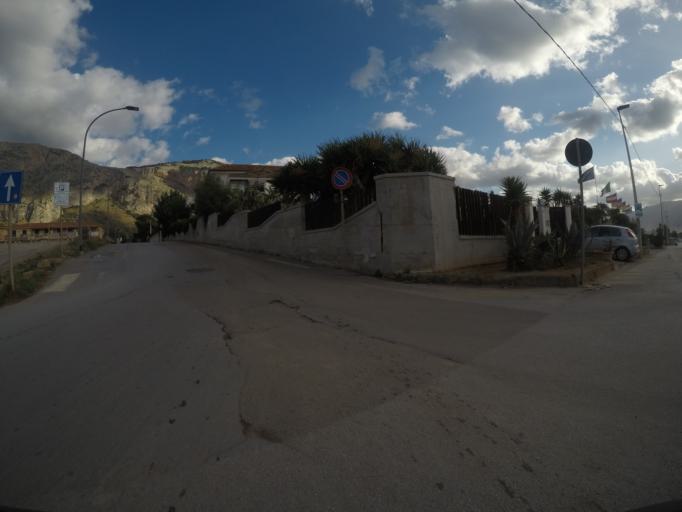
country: IT
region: Sicily
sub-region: Palermo
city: Isola delle Femmine
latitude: 38.1864
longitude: 13.2390
